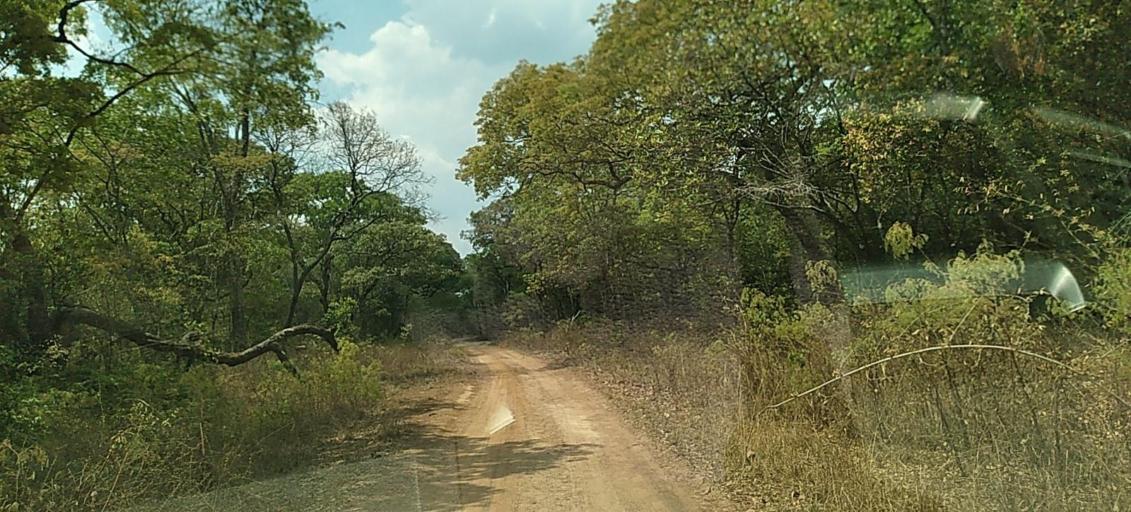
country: ZM
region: Copperbelt
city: Chingola
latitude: -12.7605
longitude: 27.7066
